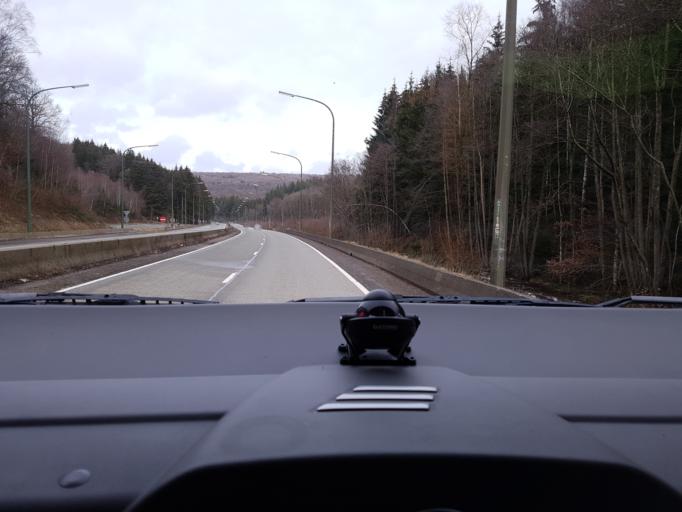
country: BE
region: Wallonia
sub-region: Province du Luxembourg
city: Tenneville
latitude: 50.1397
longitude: 5.4524
